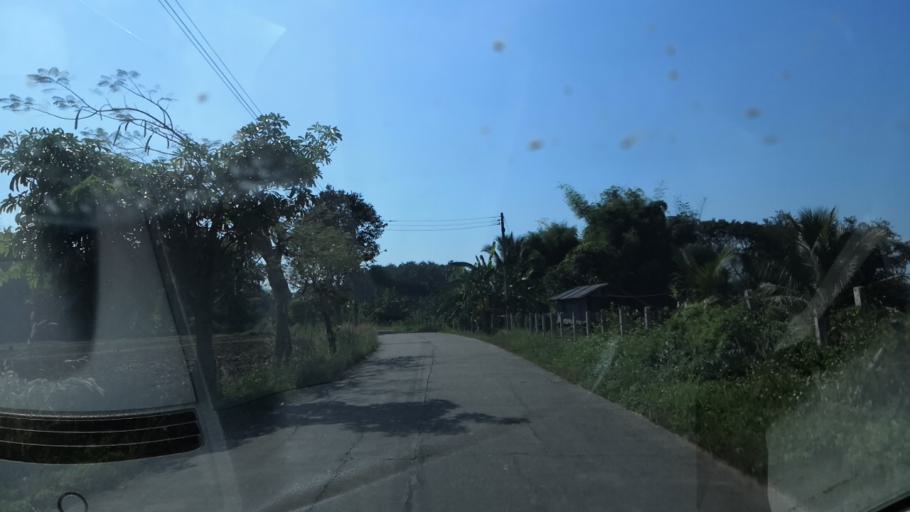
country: TH
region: Chiang Rai
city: Wiang Chai
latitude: 19.8836
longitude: 99.9429
